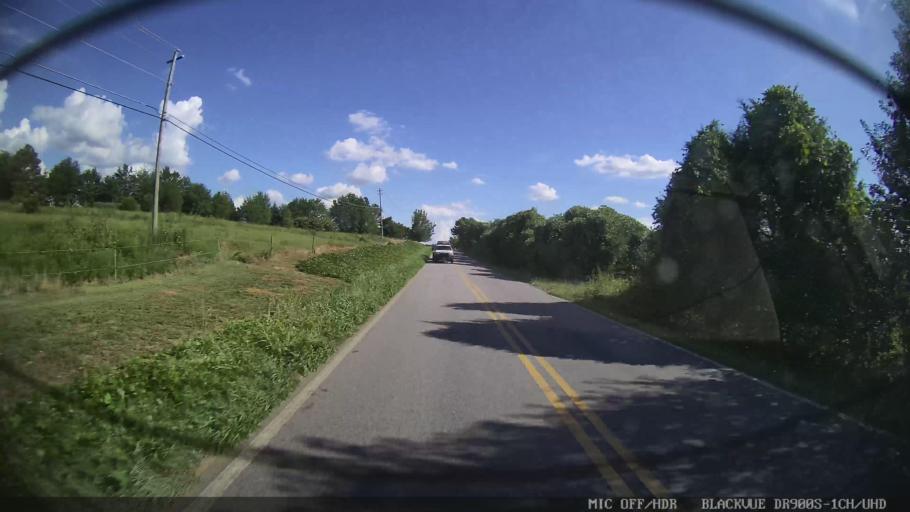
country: US
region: Georgia
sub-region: Bartow County
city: Euharlee
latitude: 34.1020
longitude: -84.9904
